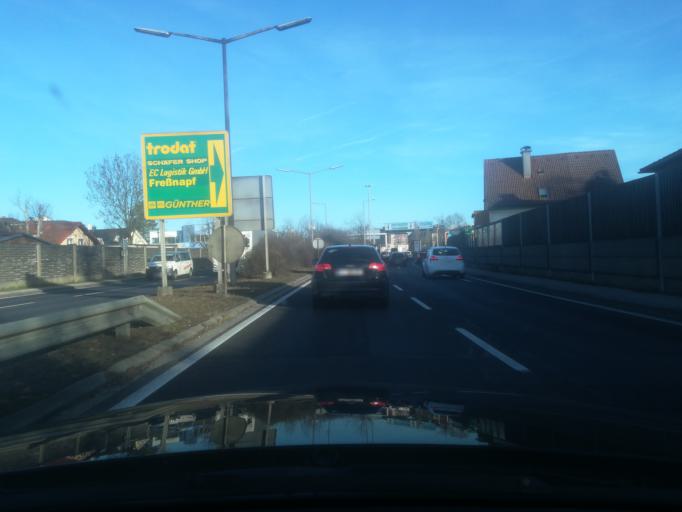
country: AT
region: Upper Austria
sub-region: Wels Stadt
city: Wels
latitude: 48.1636
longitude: 14.0410
